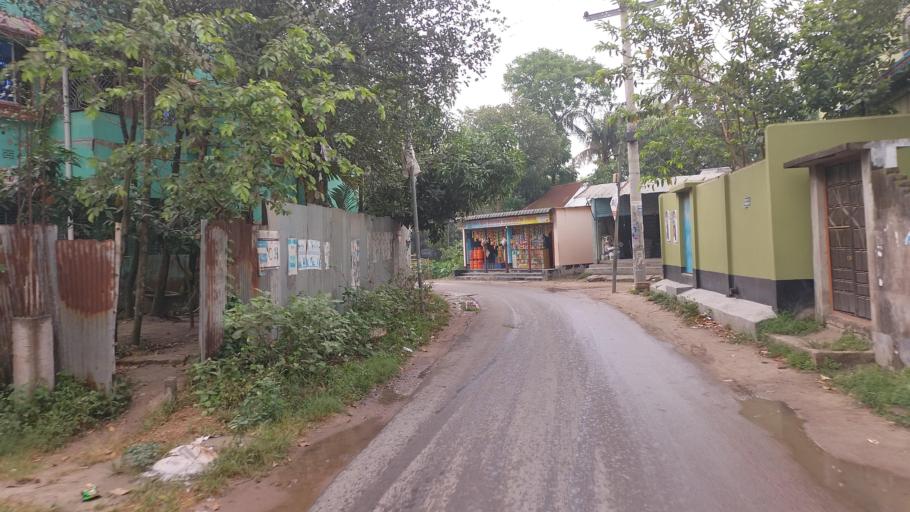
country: BD
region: Dhaka
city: Azimpur
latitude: 23.6737
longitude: 90.3465
